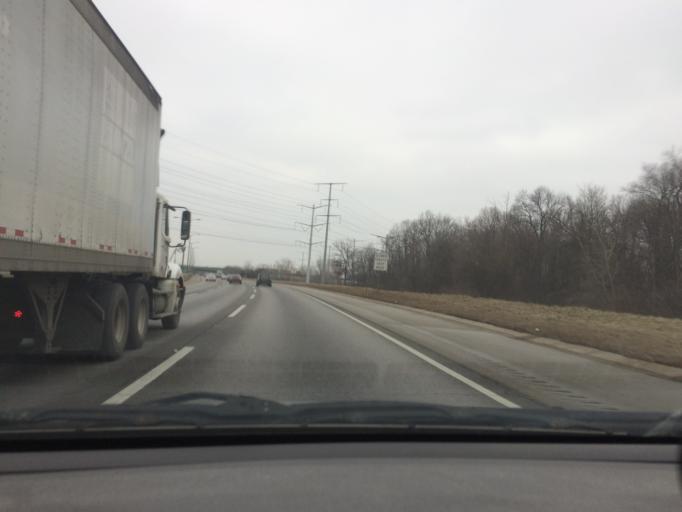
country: US
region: Illinois
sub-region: DuPage County
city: Lombard
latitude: 41.8886
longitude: -88.0374
